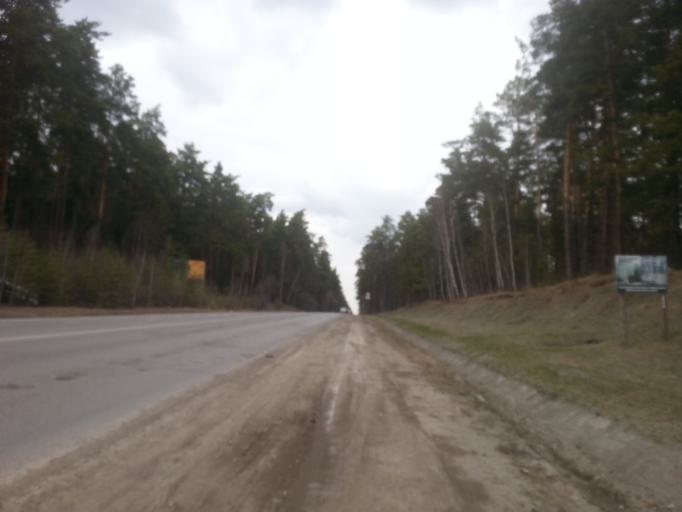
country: RU
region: Altai Krai
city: Yuzhnyy
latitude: 53.2706
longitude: 83.7247
